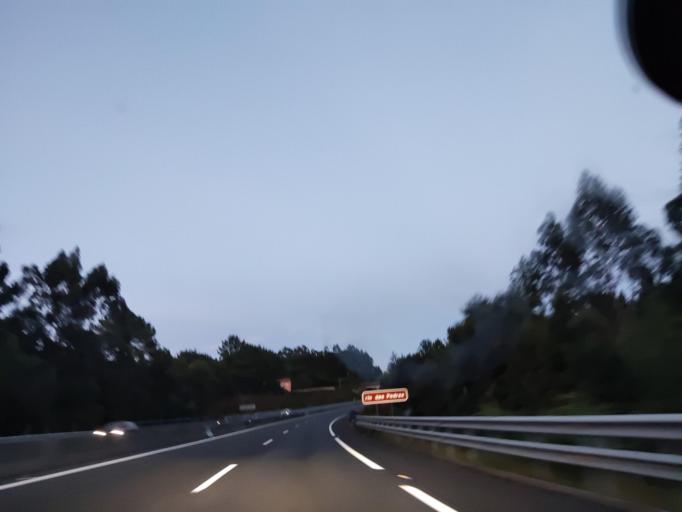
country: ES
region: Galicia
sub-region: Provincia da Coruna
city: Boiro
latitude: 42.6232
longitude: -8.9420
